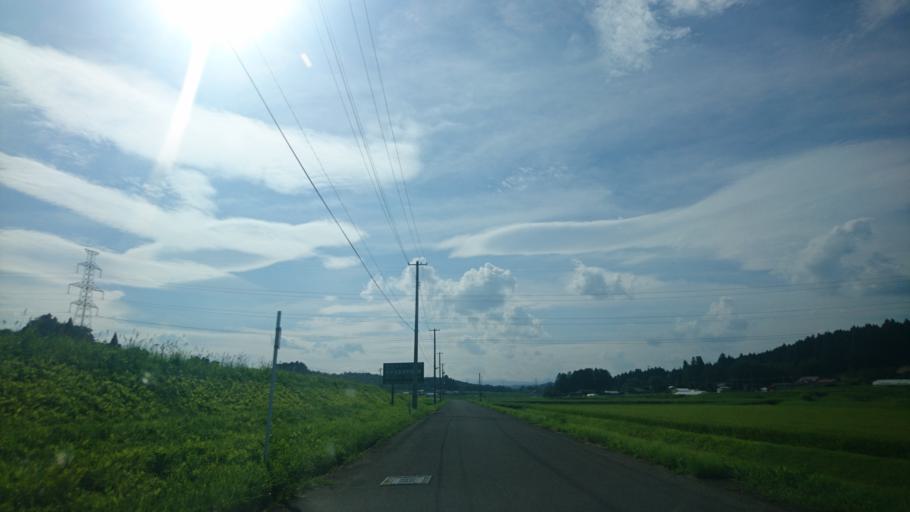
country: JP
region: Miyagi
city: Furukawa
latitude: 38.7620
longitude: 140.9785
